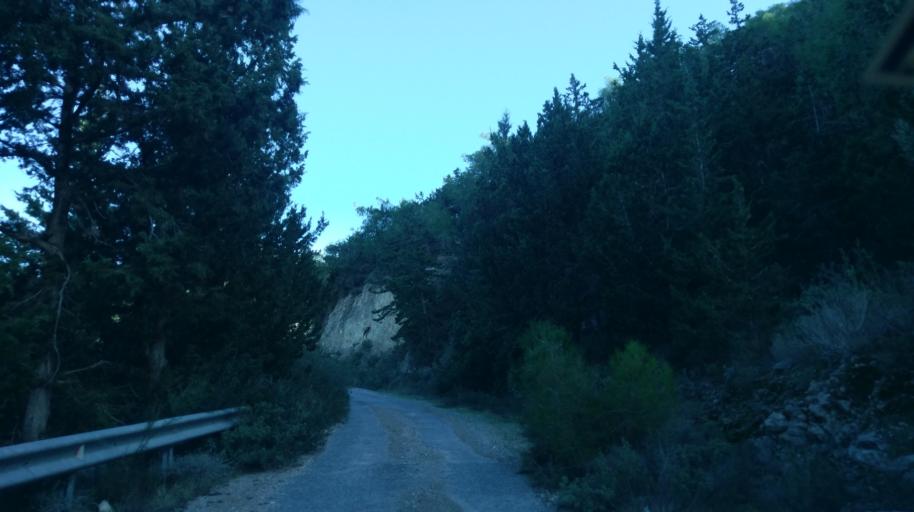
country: CY
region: Ammochostos
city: Lefkonoiko
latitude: 35.3361
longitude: 33.6334
